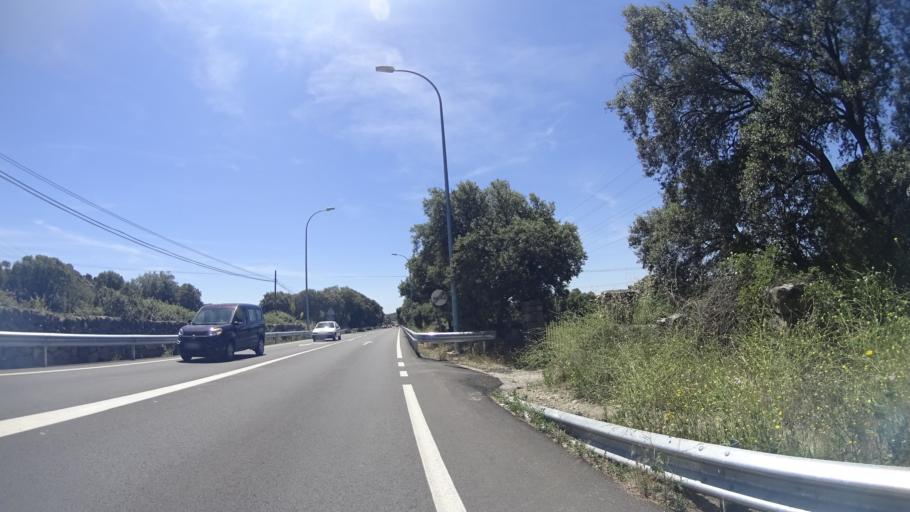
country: ES
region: Madrid
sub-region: Provincia de Madrid
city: Navalquejigo
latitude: 40.6039
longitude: -4.0211
